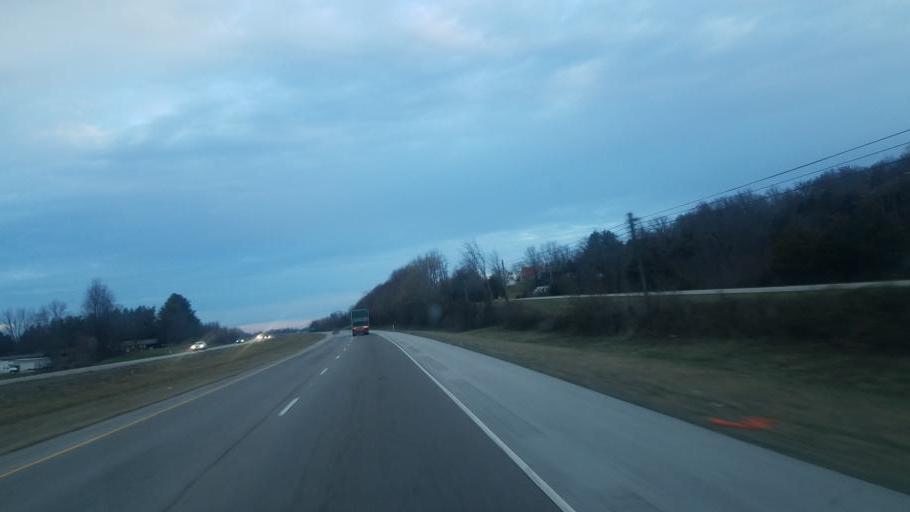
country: US
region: Tennessee
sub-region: White County
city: Sparta
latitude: 36.0062
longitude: -85.5040
